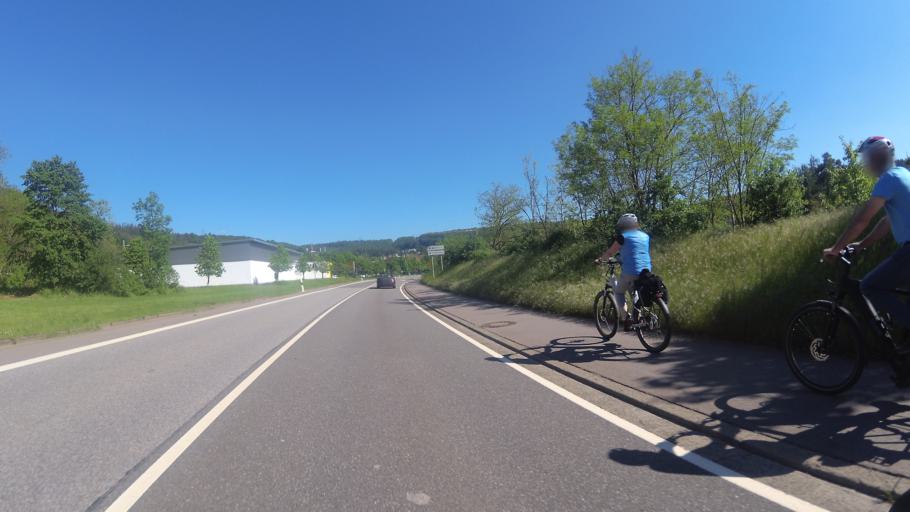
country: DE
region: Saarland
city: Mettlach
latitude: 49.4995
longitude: 6.5942
